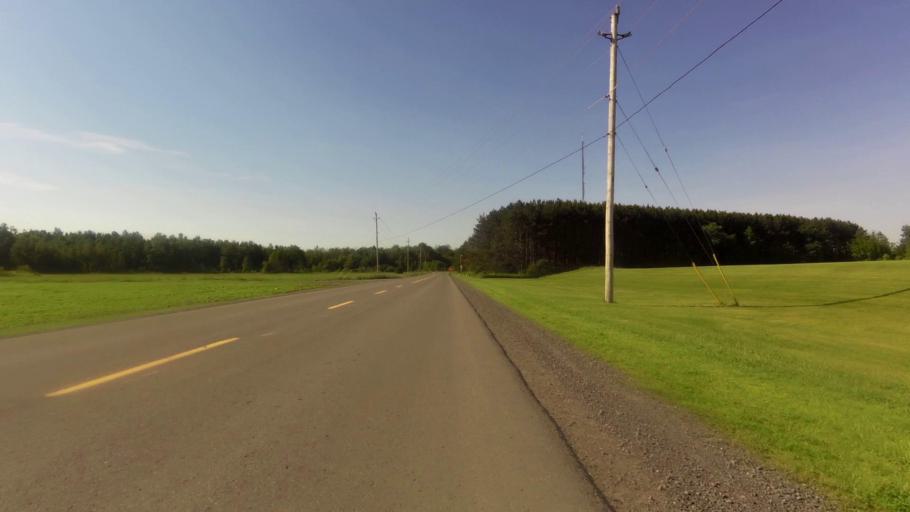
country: CA
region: Ontario
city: Ottawa
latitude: 45.2250
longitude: -75.5609
